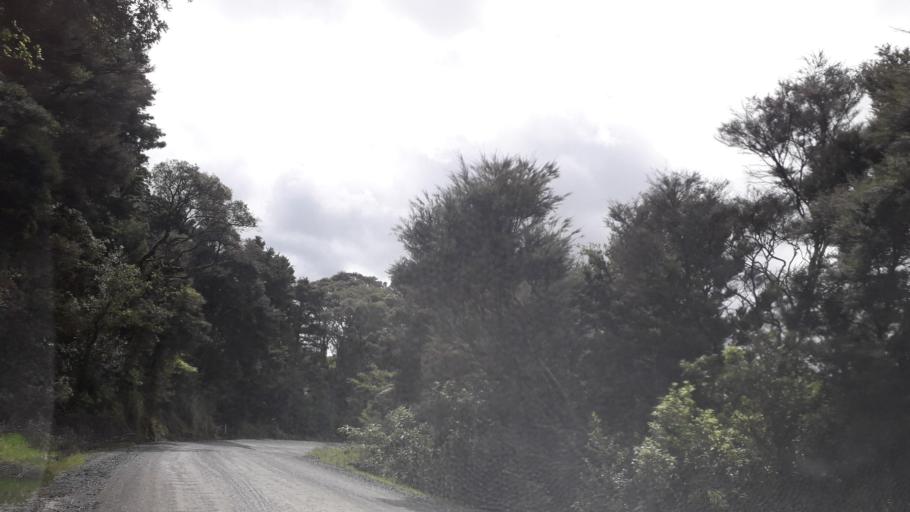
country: NZ
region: Northland
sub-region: Far North District
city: Kaitaia
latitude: -35.1712
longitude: 173.3405
